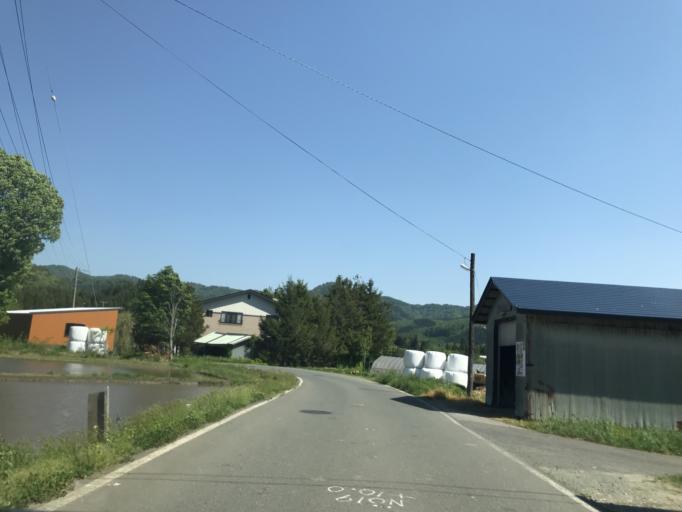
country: JP
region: Iwate
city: Shizukuishi
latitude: 39.5573
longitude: 140.8425
